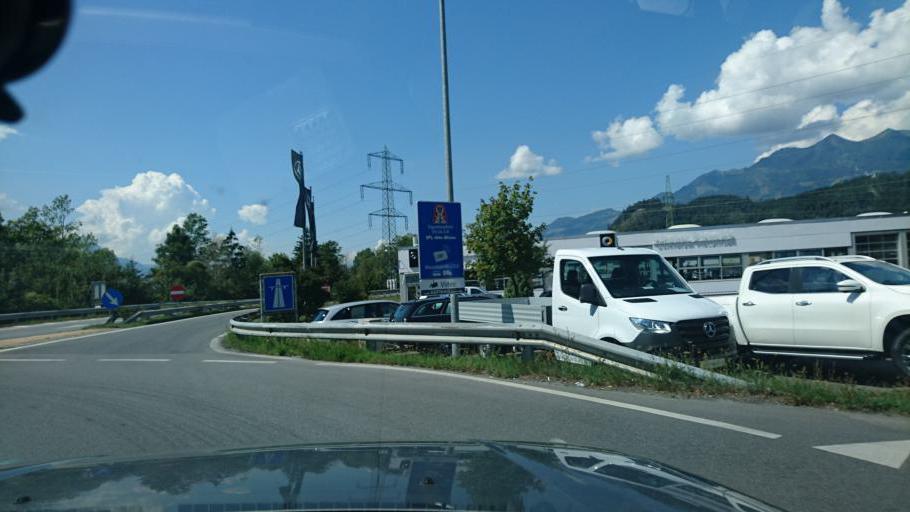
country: AT
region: Vorarlberg
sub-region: Politischer Bezirk Bludenz
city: Nuziders
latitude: 47.1663
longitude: 9.7923
